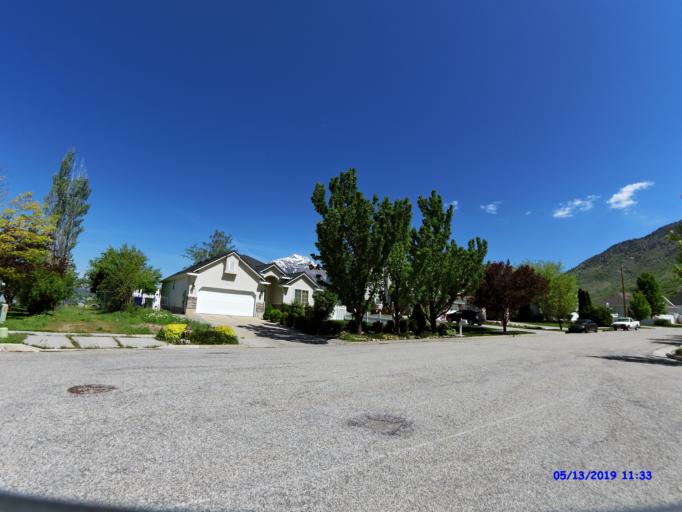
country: US
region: Utah
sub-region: Weber County
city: North Ogden
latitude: 41.2784
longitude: -111.9544
